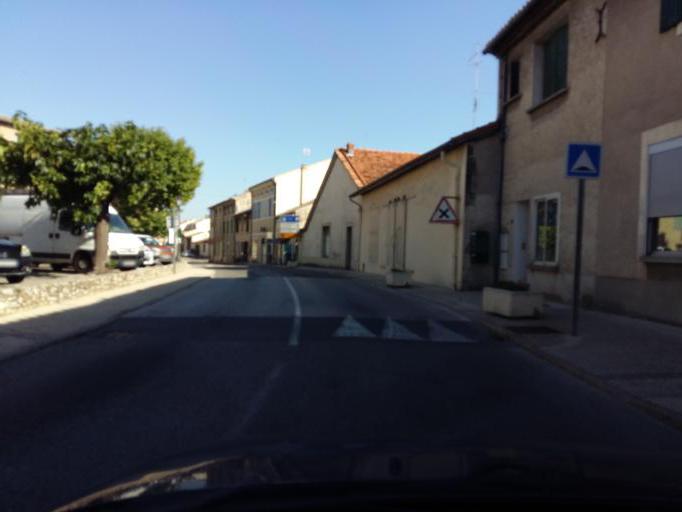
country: FR
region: Provence-Alpes-Cote d'Azur
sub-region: Departement du Vaucluse
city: Visan
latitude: 44.3139
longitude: 4.9494
